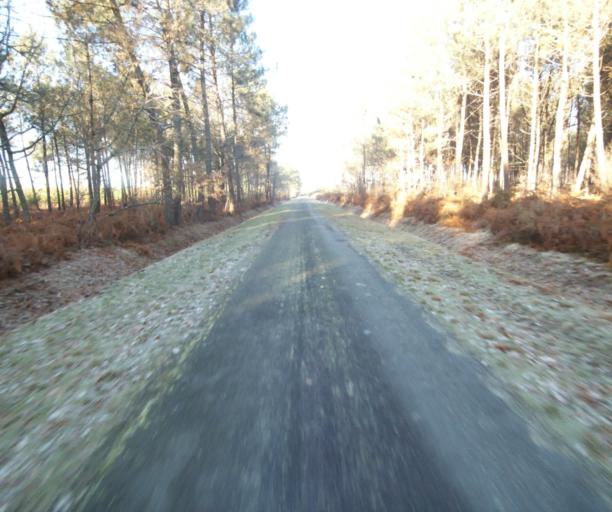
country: FR
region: Aquitaine
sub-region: Departement des Landes
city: Gabarret
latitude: 44.1145
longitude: 0.0377
